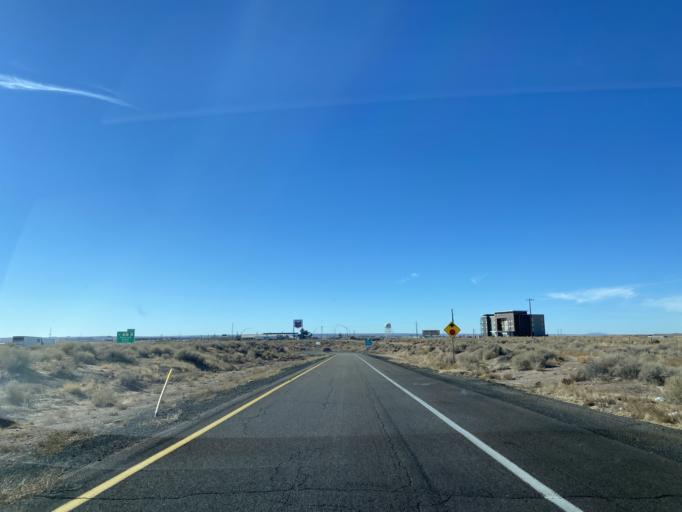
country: US
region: Arizona
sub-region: Navajo County
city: Holbrook
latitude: 34.9408
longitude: -110.1287
